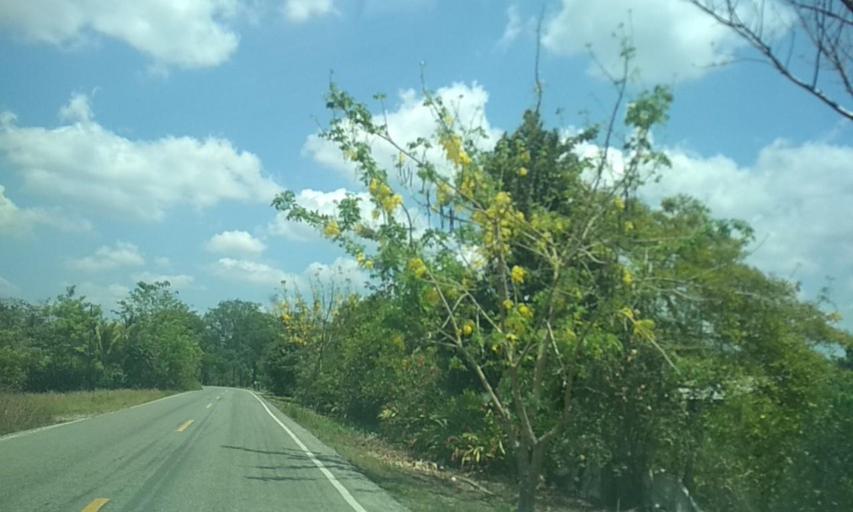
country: MX
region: Tabasco
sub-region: Huimanguillo
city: Huapacal 1ra. Seccion
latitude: 17.7527
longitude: -93.7301
